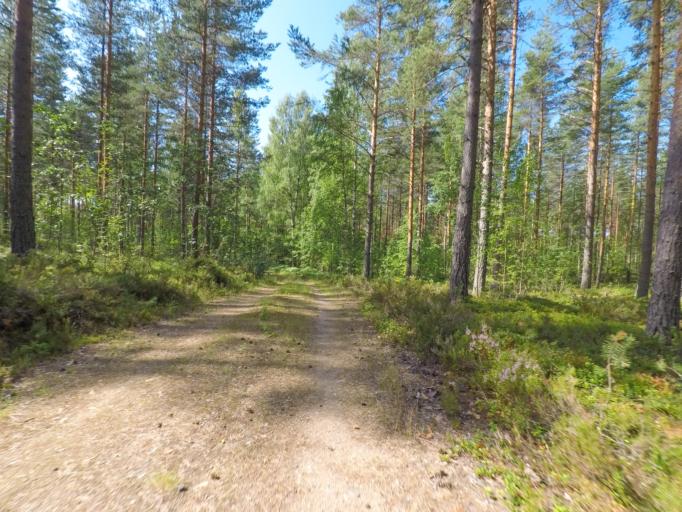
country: FI
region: Southern Savonia
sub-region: Mikkeli
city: Puumala
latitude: 61.5158
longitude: 28.1667
